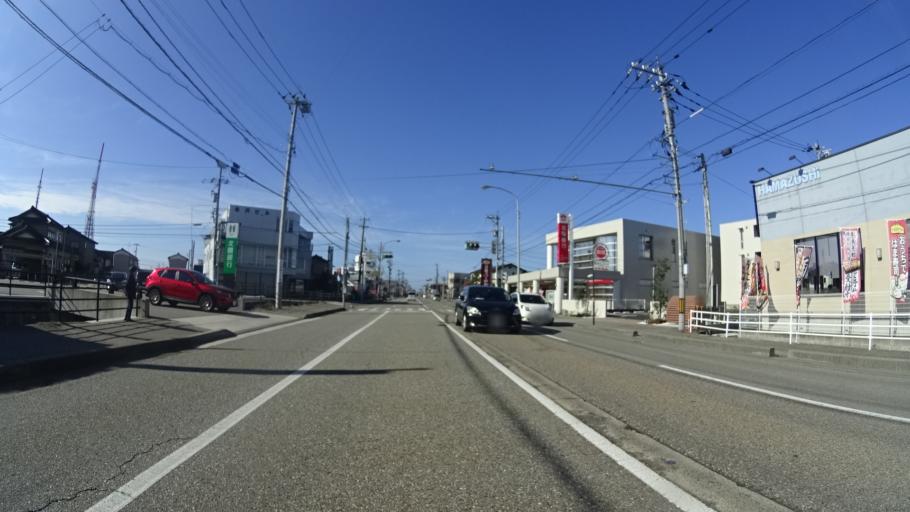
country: JP
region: Ishikawa
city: Kanazawa-shi
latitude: 36.5905
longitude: 136.6139
